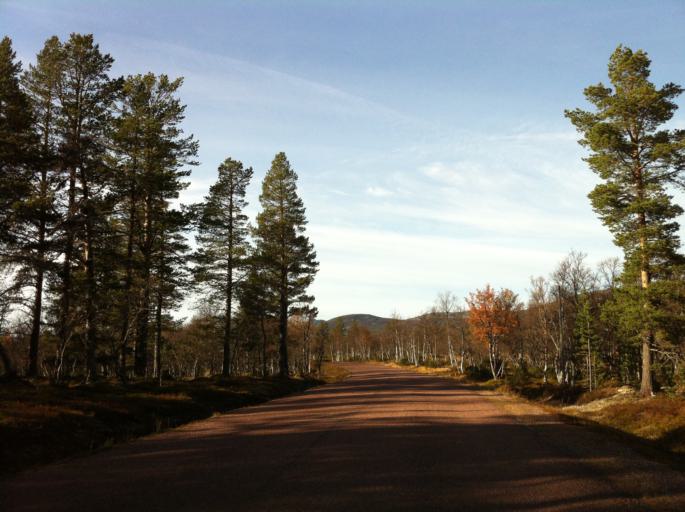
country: NO
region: Hedmark
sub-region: Engerdal
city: Engerdal
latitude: 62.0697
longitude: 12.2083
